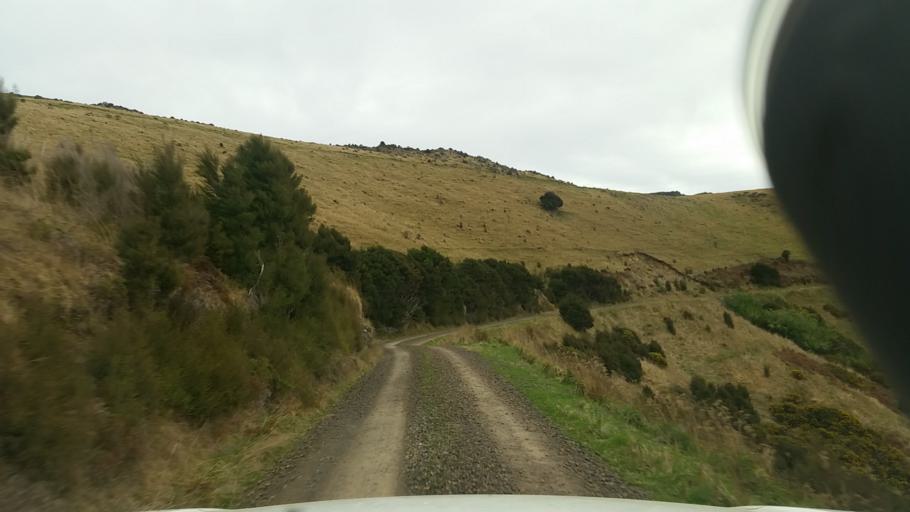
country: NZ
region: Canterbury
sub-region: Christchurch City
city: Christchurch
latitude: -43.8424
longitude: 173.0109
